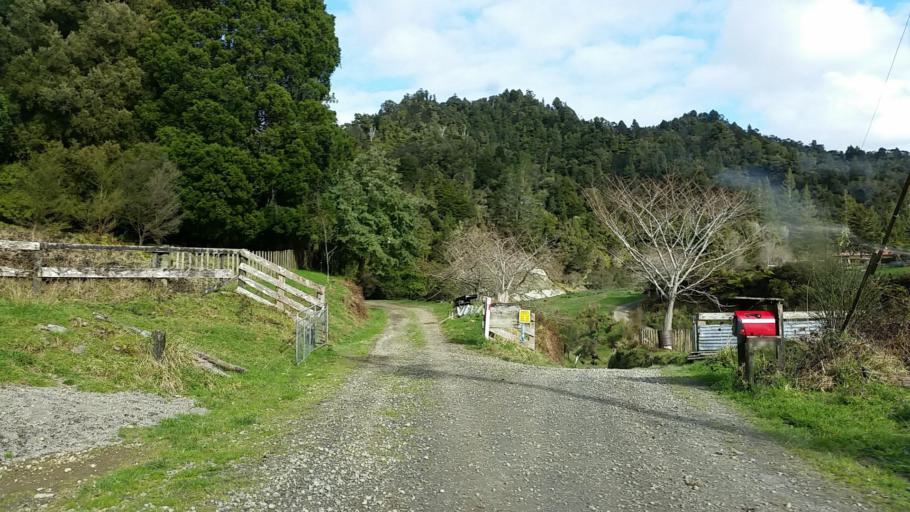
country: NZ
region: Taranaki
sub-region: New Plymouth District
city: Waitara
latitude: -39.0977
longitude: 174.5643
